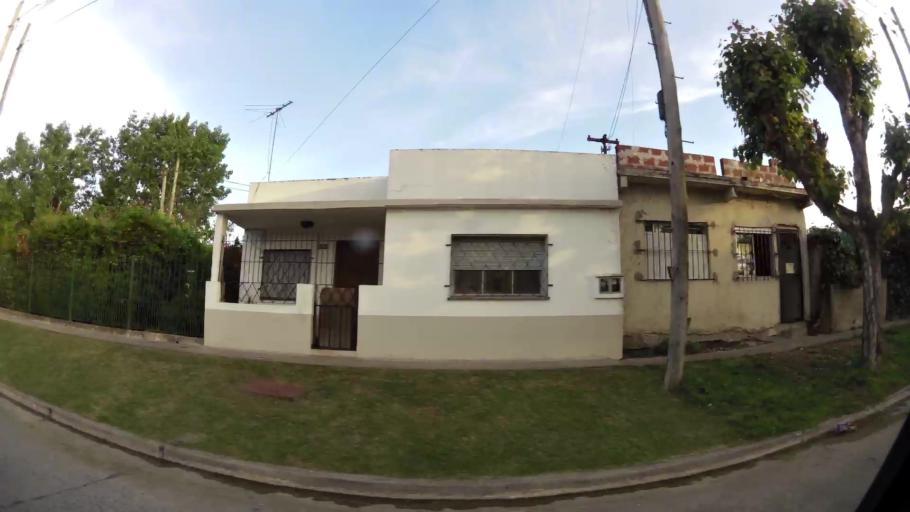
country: AR
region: Buenos Aires
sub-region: Partido de Quilmes
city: Quilmes
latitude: -34.7770
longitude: -58.2027
